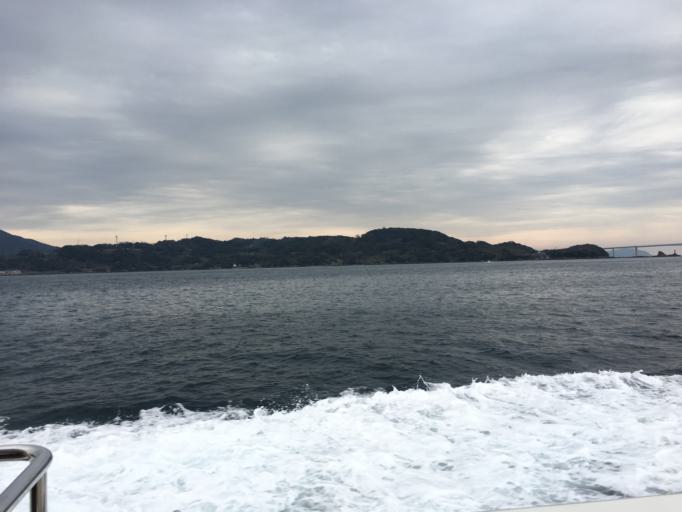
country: JP
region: Nagasaki
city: Nagasaki-shi
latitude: 32.7068
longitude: 129.7973
